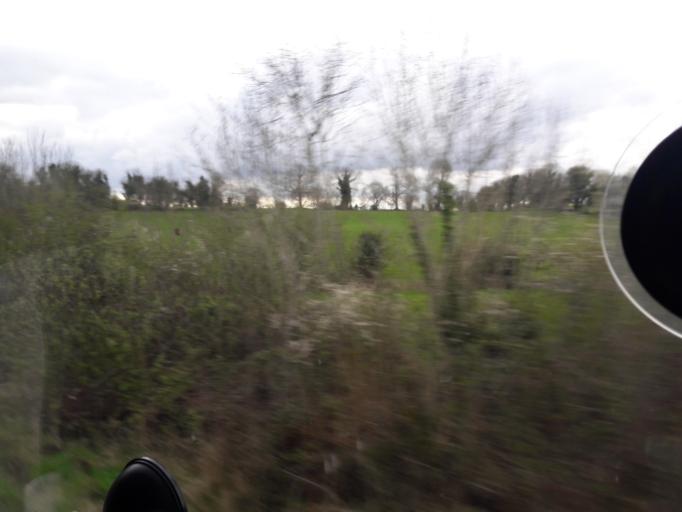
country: IE
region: Leinster
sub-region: An Longfort
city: Longford
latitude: 53.7451
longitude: -7.8234
